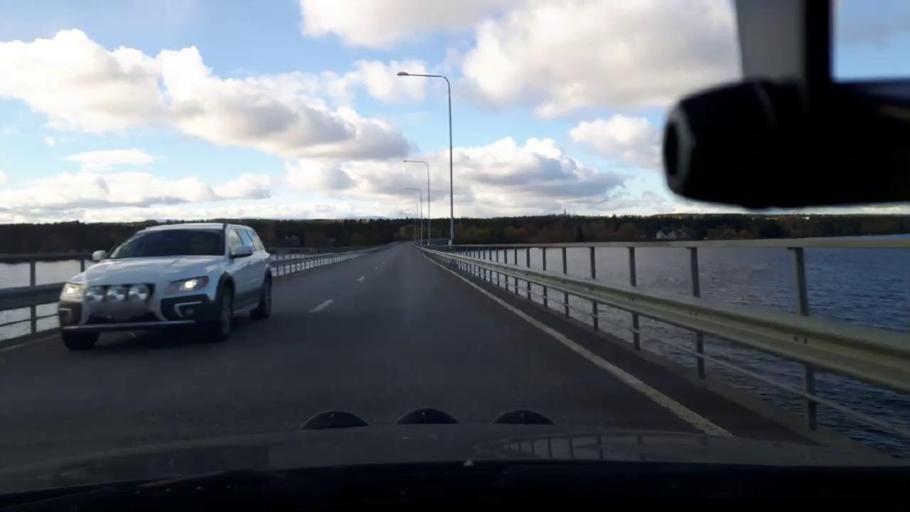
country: SE
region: Jaemtland
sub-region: Bergs Kommun
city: Hoverberg
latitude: 62.9777
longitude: 14.4671
